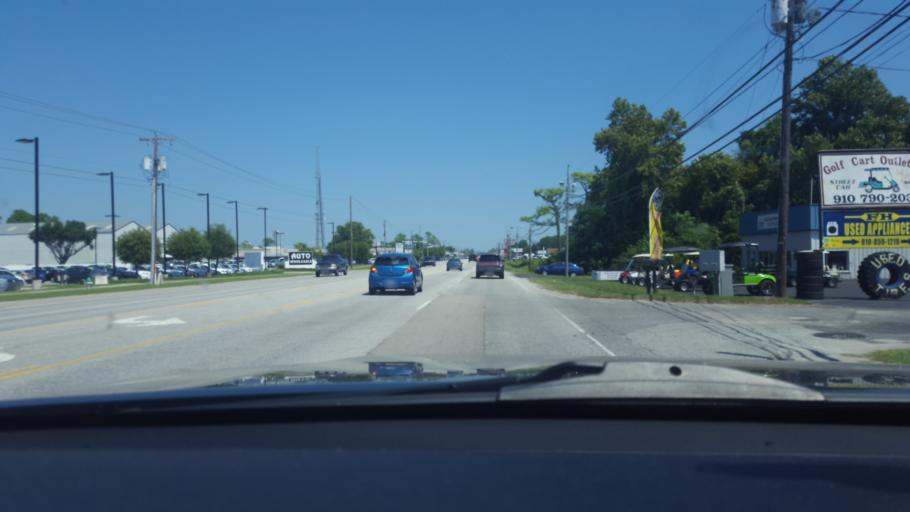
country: US
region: North Carolina
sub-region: New Hanover County
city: Kings Grant
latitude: 34.2515
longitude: -77.8541
